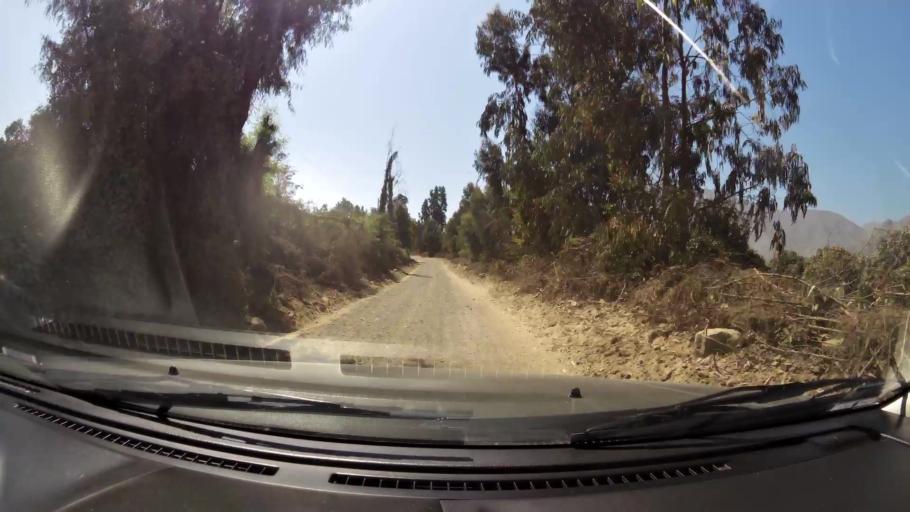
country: PE
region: Ica
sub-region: Provincia de Ica
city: Guadalupe
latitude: -13.8775
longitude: -75.6440
